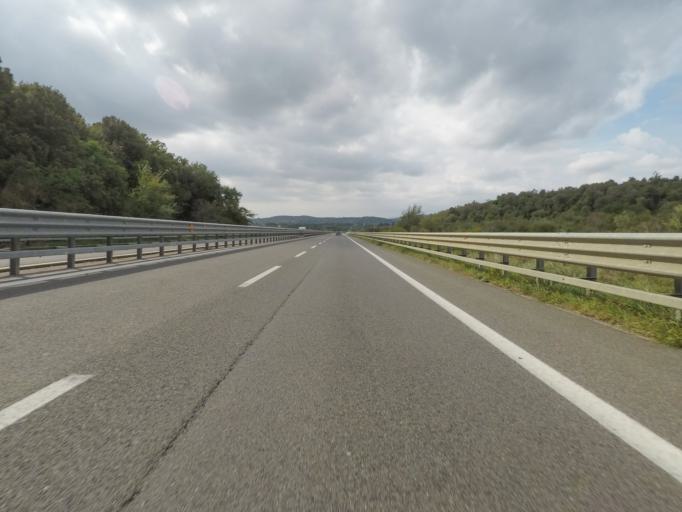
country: IT
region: Tuscany
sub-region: Provincia di Grosseto
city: Bagno Roselle
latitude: 42.8561
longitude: 11.1773
